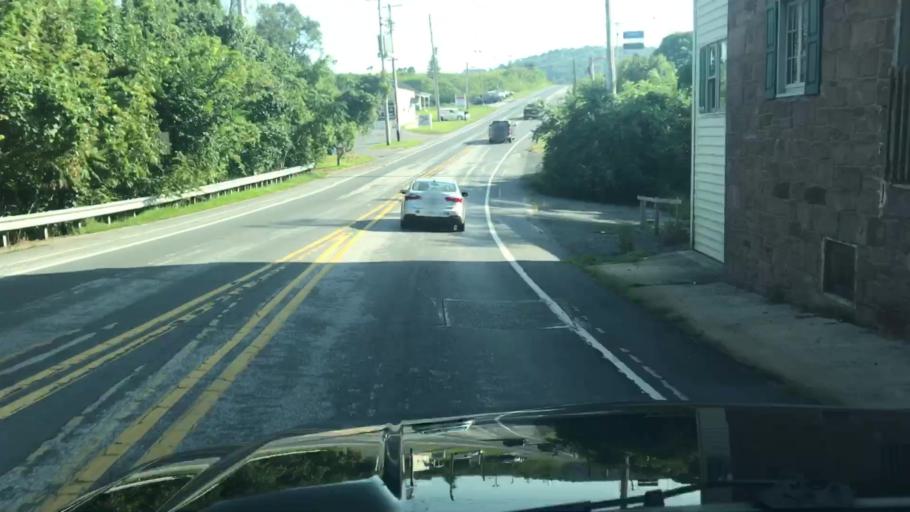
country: US
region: Pennsylvania
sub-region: York County
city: Valley Green
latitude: 40.1588
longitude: -76.8161
